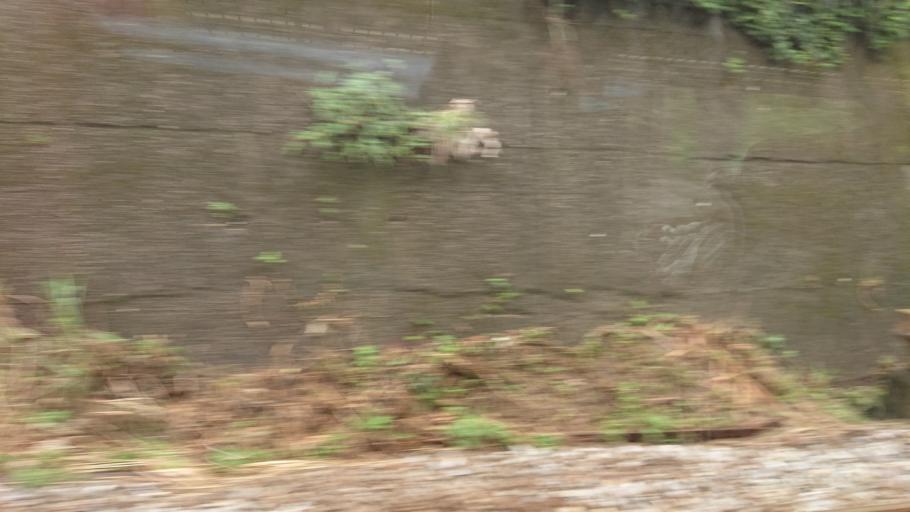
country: TW
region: Taiwan
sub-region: Keelung
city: Keelung
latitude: 25.0981
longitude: 121.8327
